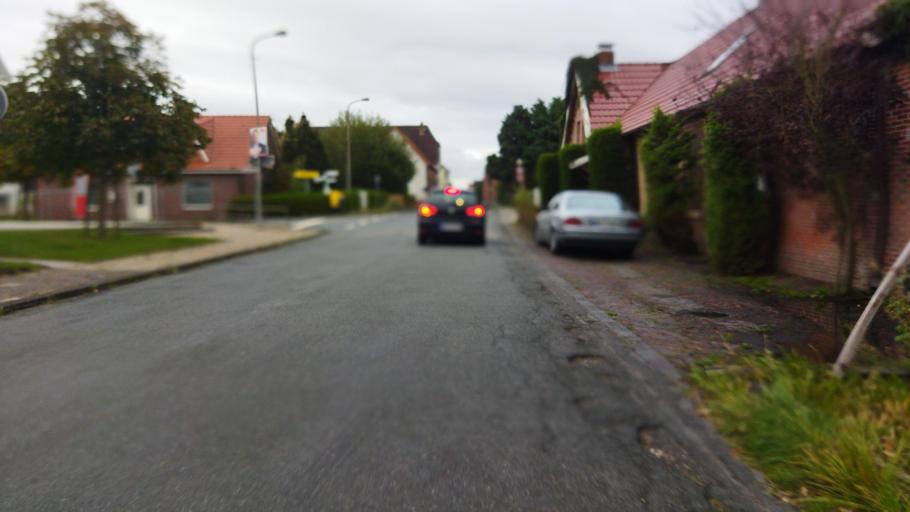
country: DE
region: Lower Saxony
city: Hinte
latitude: 53.4167
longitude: 7.1929
